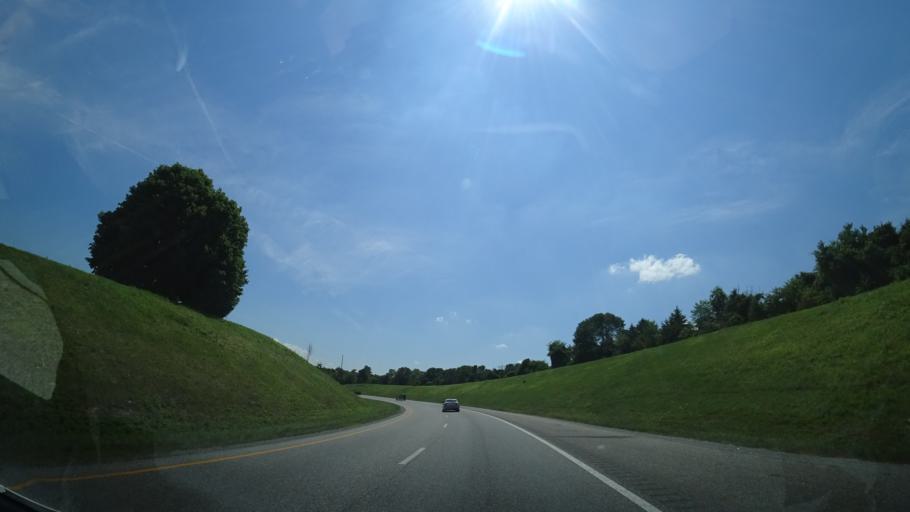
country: US
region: Virginia
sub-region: Augusta County
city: Jolivue
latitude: 38.1235
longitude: -79.0464
